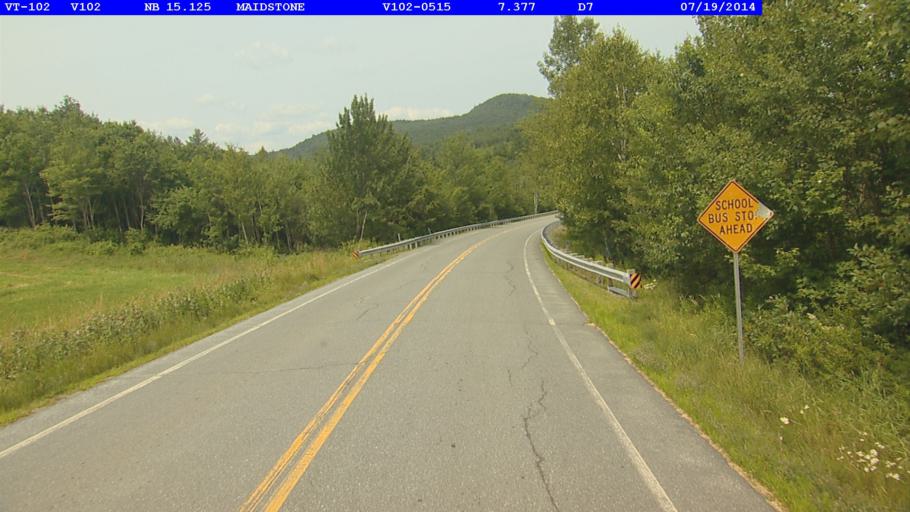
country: US
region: New Hampshire
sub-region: Coos County
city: Stratford
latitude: 44.6564
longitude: -71.5901
